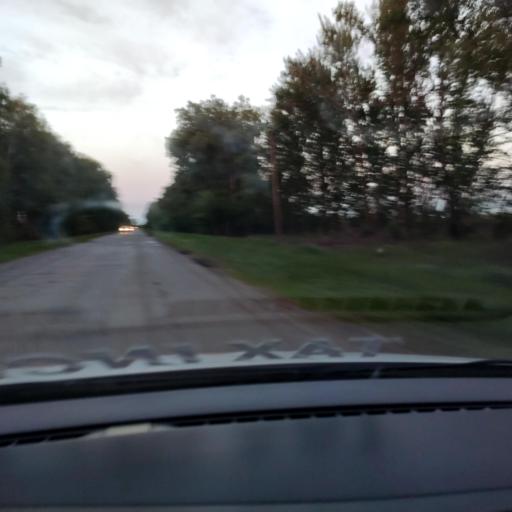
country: RU
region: Voronezj
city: Maslovka
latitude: 51.4389
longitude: 39.2909
